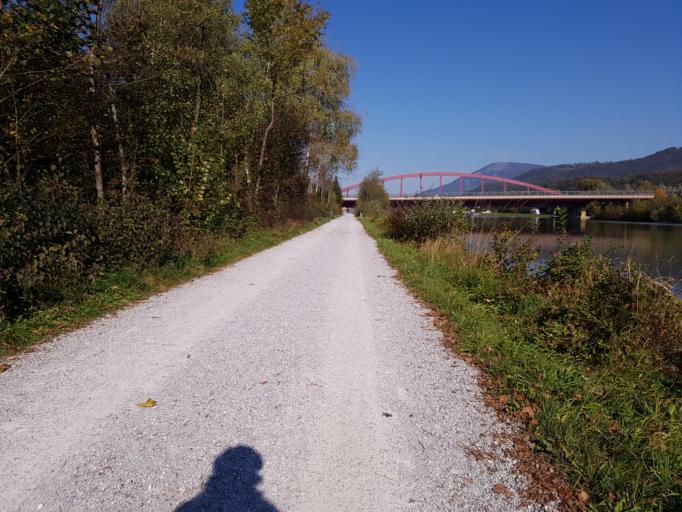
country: AT
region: Salzburg
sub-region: Politischer Bezirk Hallein
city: Puch bei Hallein
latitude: 47.7290
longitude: 13.0823
